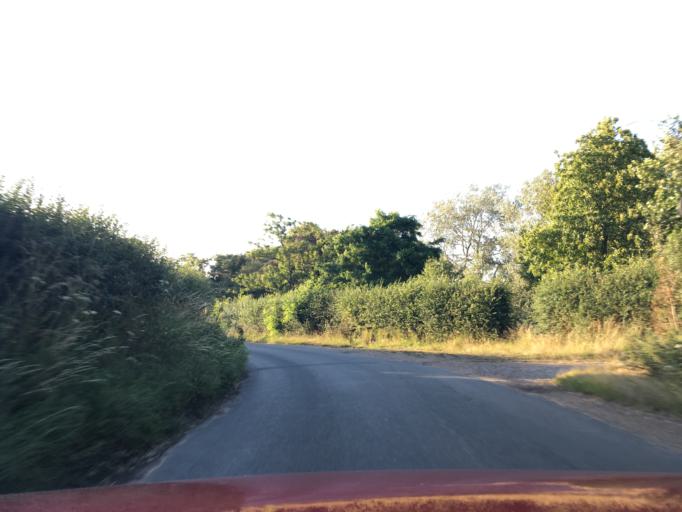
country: GB
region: England
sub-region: West Berkshire
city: Cold Ash
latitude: 51.4328
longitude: -1.2045
